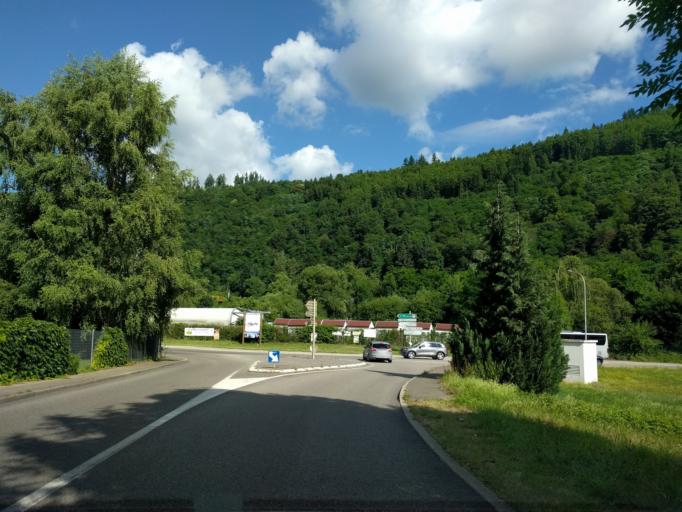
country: FR
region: Alsace
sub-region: Departement du Haut-Rhin
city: Sainte-Marie-aux-Mines
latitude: 48.2539
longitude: 7.2009
